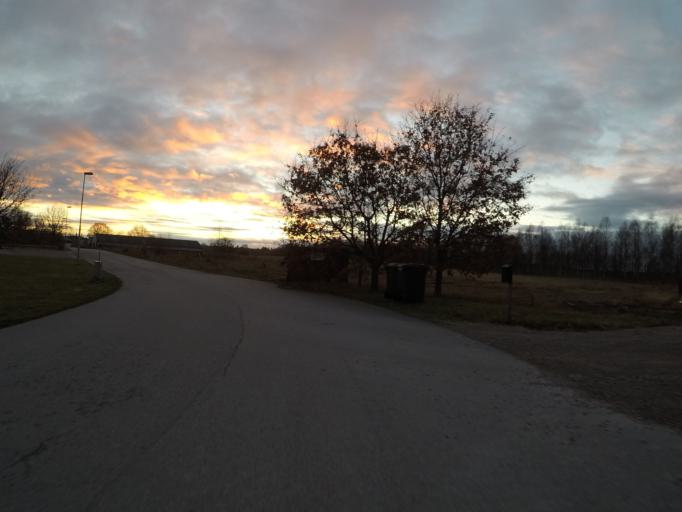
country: SE
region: Skane
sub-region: Sjobo Kommun
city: Sjoebo
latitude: 55.6458
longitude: 13.6933
